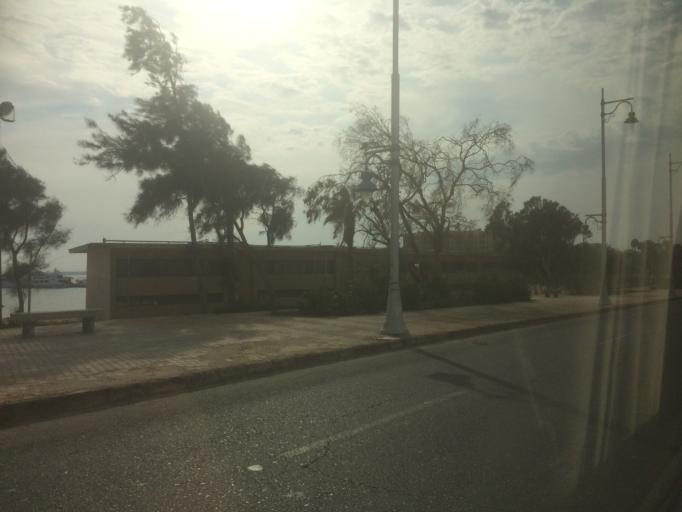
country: EG
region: Red Sea
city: Hurghada
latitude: 27.1986
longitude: 33.8475
